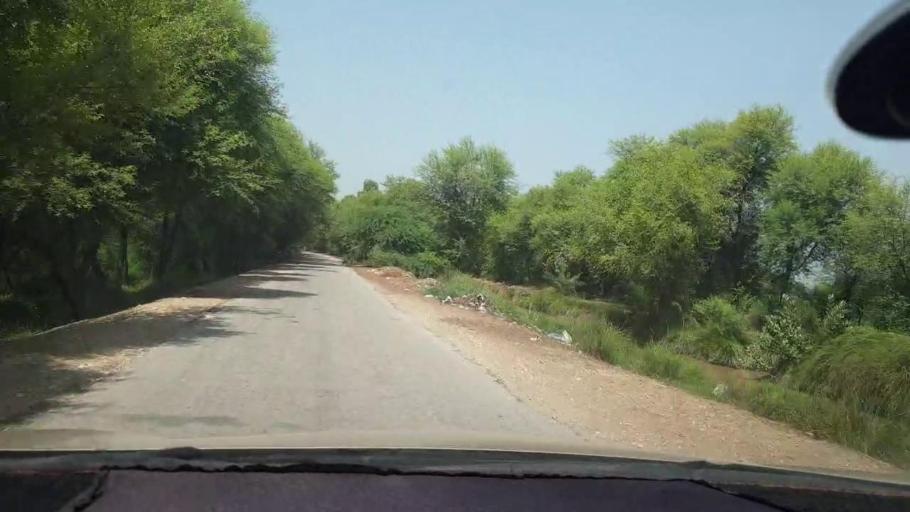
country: PK
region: Sindh
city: Kambar
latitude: 27.6552
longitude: 67.9616
